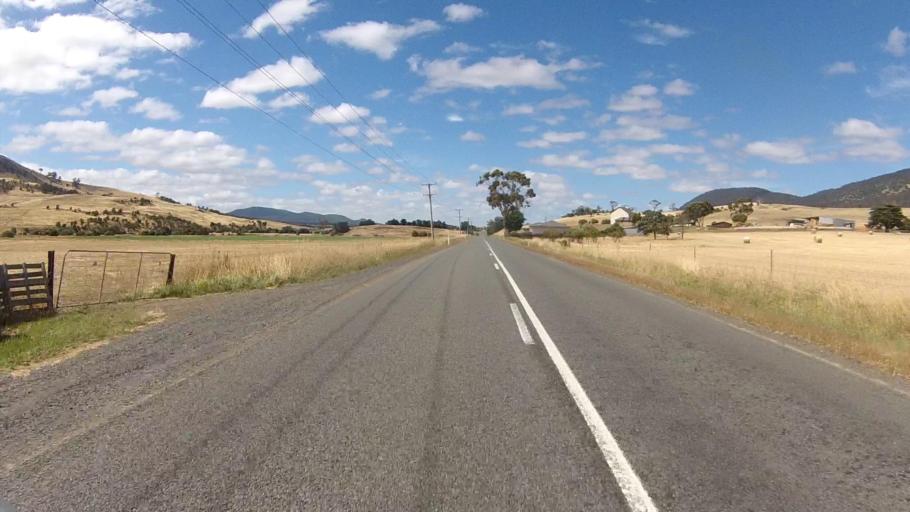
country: AU
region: Tasmania
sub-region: Brighton
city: Bridgewater
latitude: -42.5906
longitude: 147.4102
